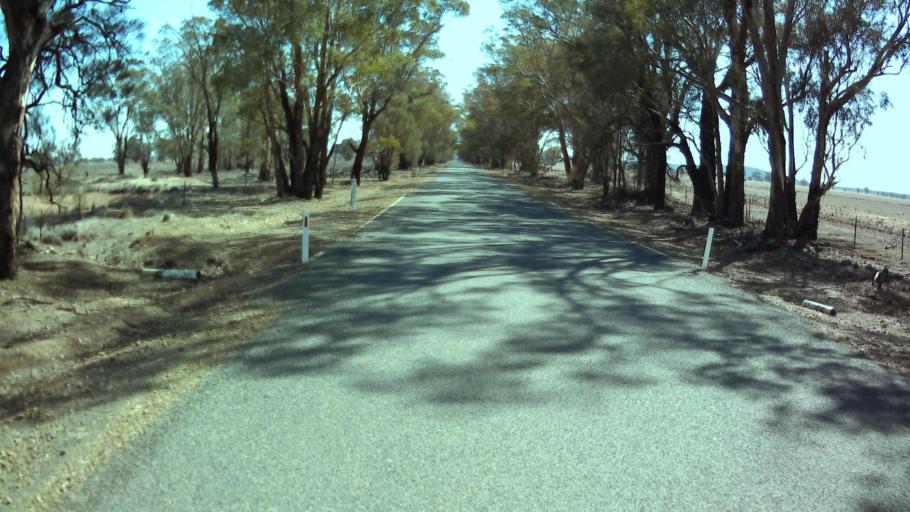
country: AU
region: New South Wales
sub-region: Weddin
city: Grenfell
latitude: -33.7254
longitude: 147.8944
